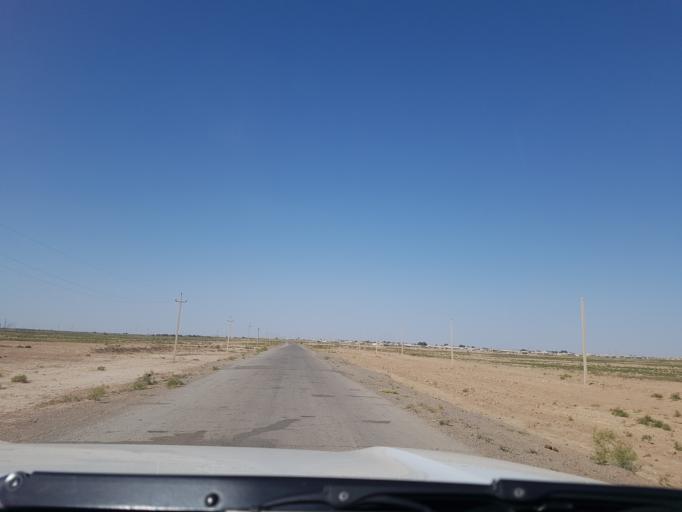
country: IR
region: Razavi Khorasan
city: Sarakhs
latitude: 36.4986
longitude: 61.2537
